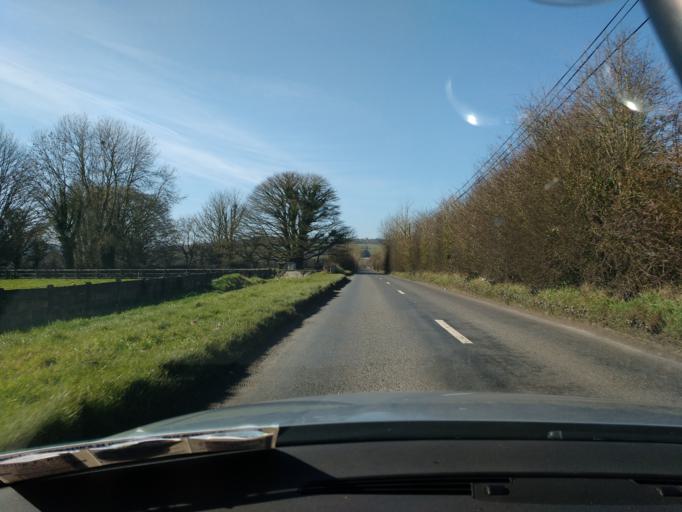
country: IE
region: Munster
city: Thurles
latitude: 52.6906
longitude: -7.9226
